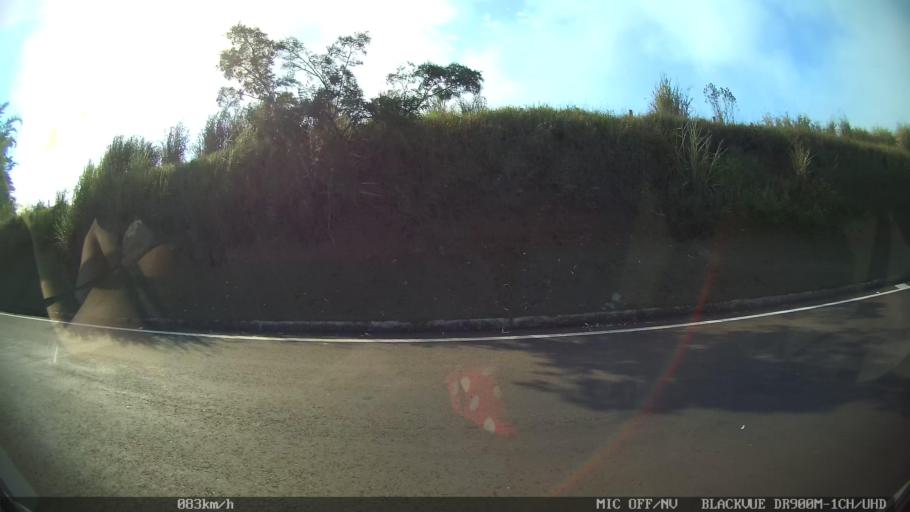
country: BR
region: Sao Paulo
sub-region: Piracicaba
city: Piracicaba
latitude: -22.7004
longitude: -47.5989
